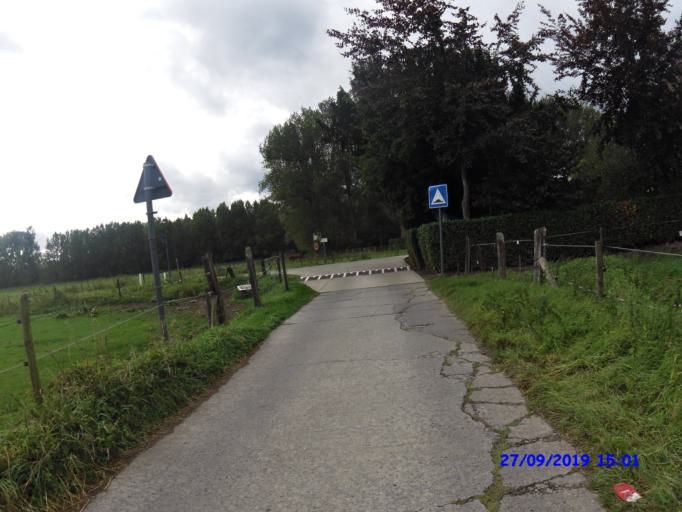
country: BE
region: Flanders
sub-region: Provincie Oost-Vlaanderen
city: Aalst
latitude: 50.9534
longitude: 4.0167
